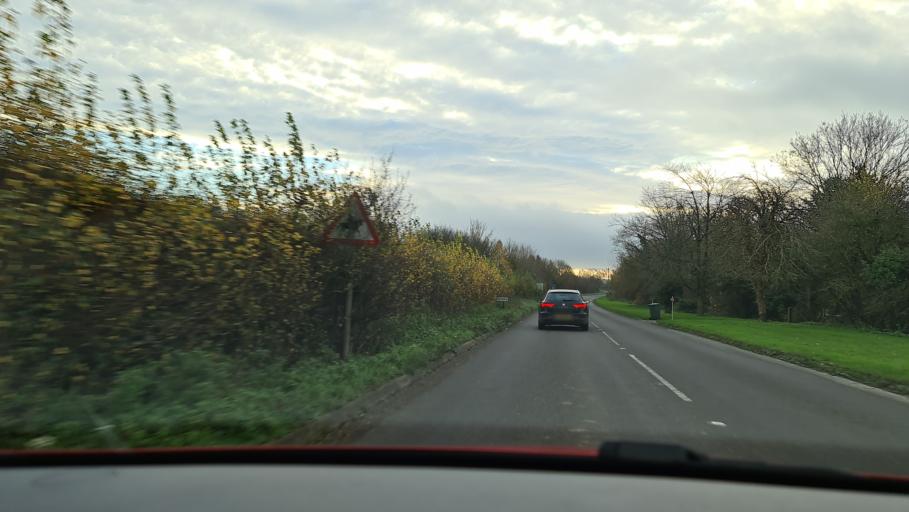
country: GB
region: England
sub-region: Oxfordshire
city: Bicester
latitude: 51.8714
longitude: -1.1054
